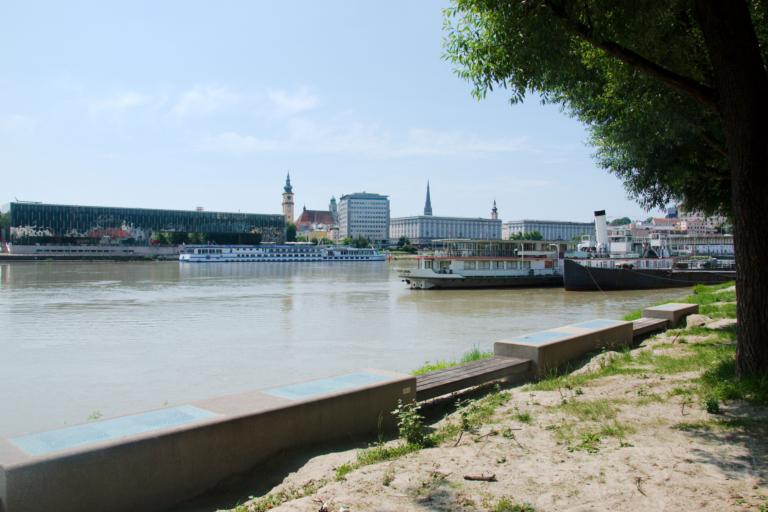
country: AT
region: Upper Austria
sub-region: Linz Stadt
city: Linz
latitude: 48.3111
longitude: 14.2874
